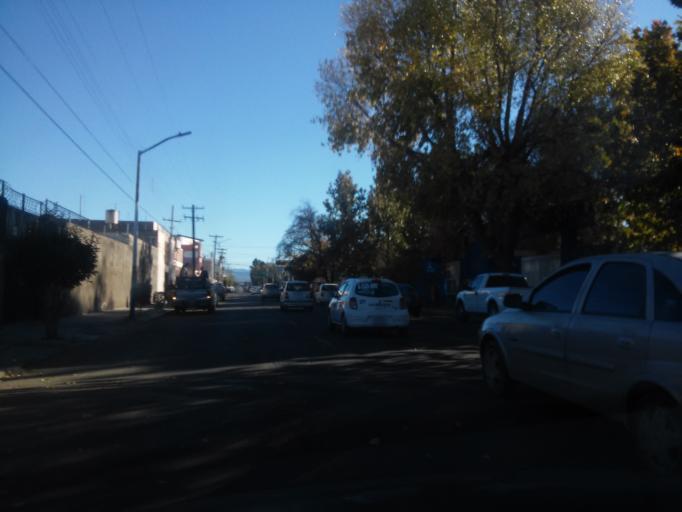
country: MX
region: Durango
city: Victoria de Durango
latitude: 24.0311
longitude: -104.6567
